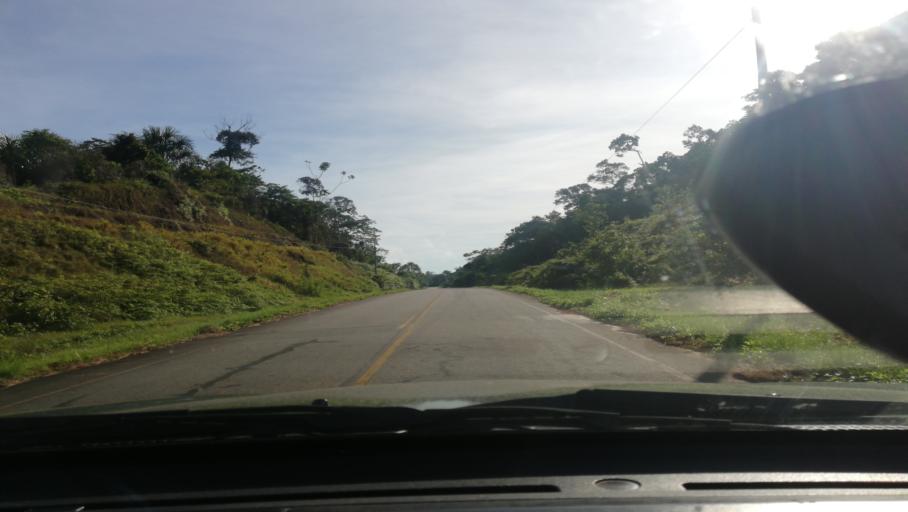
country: PE
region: Loreto
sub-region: Provincia de Loreto
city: Nauta
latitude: -4.3900
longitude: -73.5697
